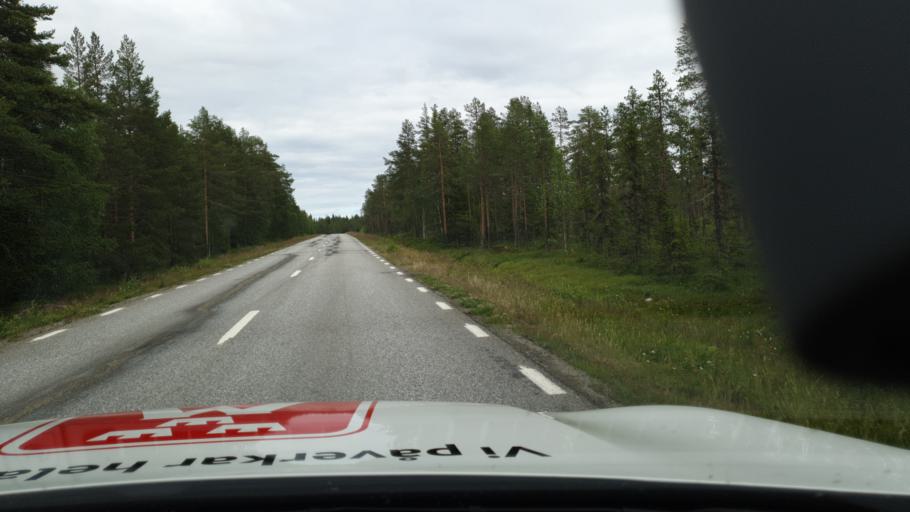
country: SE
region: Vaesterbotten
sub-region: Lycksele Kommun
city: Soderfors
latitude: 64.6240
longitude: 18.0982
